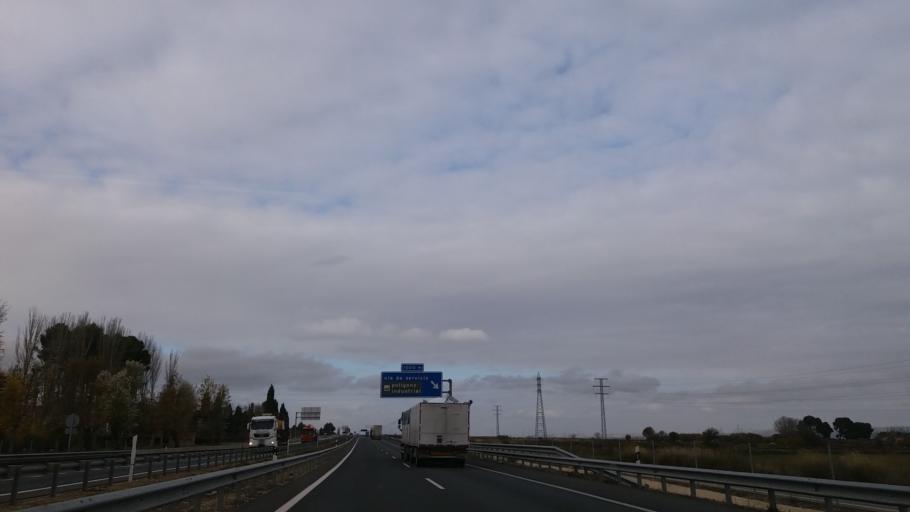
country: ES
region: Navarre
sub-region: Provincia de Navarra
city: Cortes
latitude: 41.9206
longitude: -1.4444
